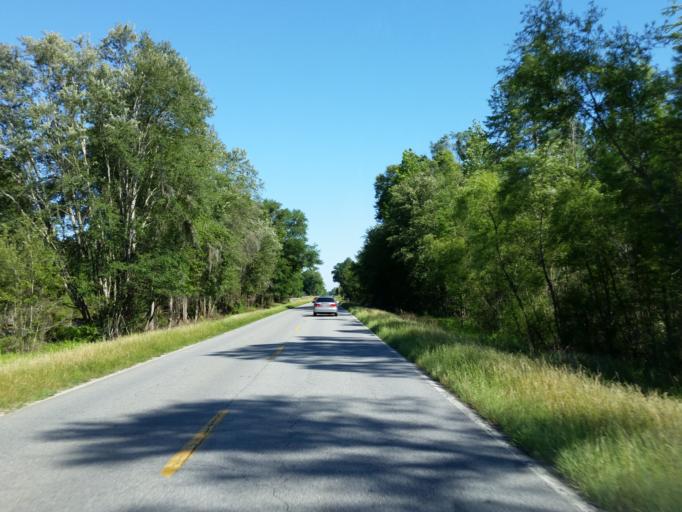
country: US
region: Georgia
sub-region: Echols County
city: Statenville
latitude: 30.6457
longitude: -83.1403
